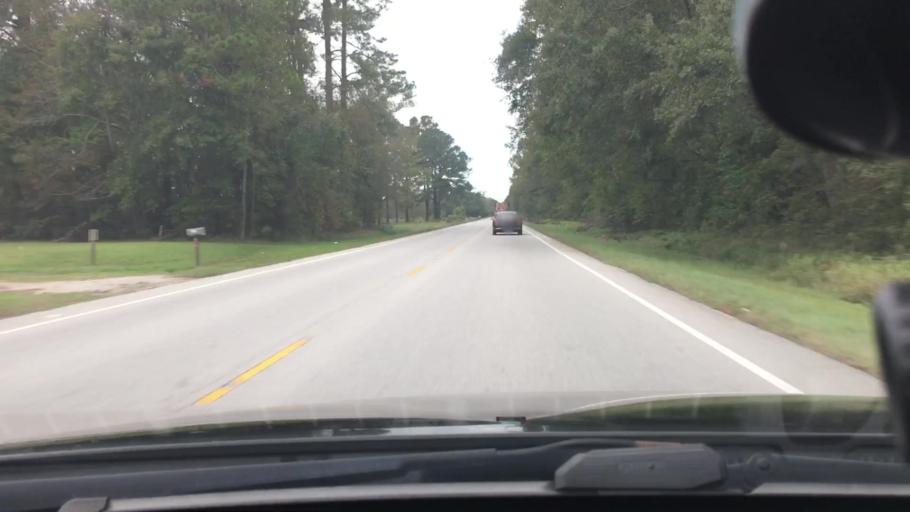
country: US
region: North Carolina
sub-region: Craven County
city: New Bern
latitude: 35.1680
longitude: -77.0418
